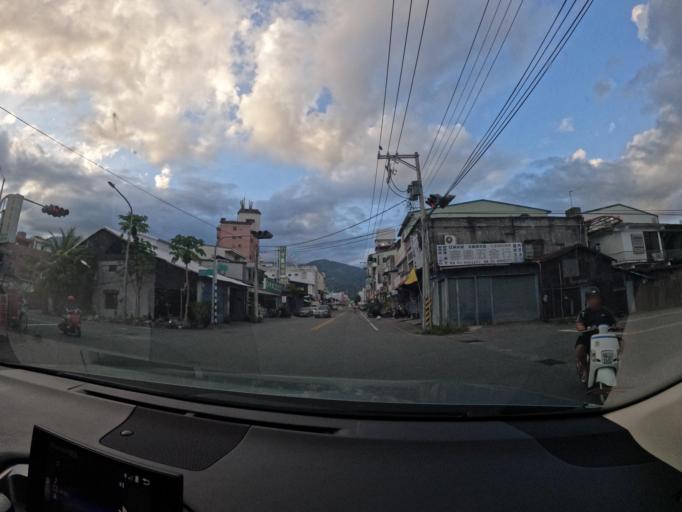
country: TW
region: Taiwan
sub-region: Taitung
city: Taitung
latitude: 23.3305
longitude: 121.3160
